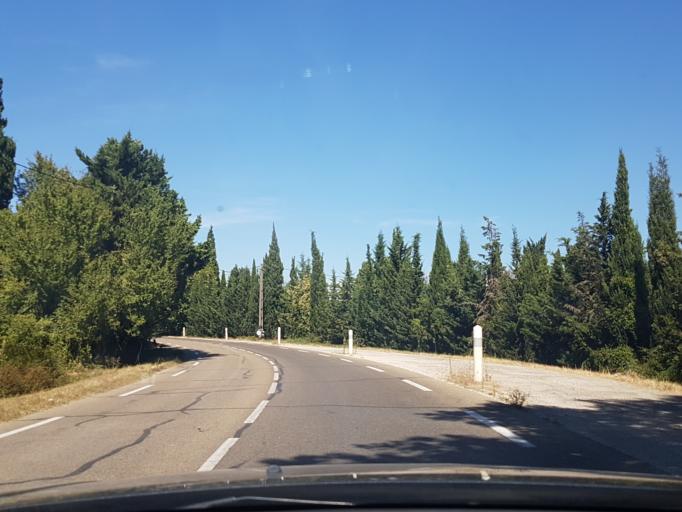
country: FR
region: Provence-Alpes-Cote d'Azur
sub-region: Departement des Bouches-du-Rhone
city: Eyragues
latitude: 43.8505
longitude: 4.8413
